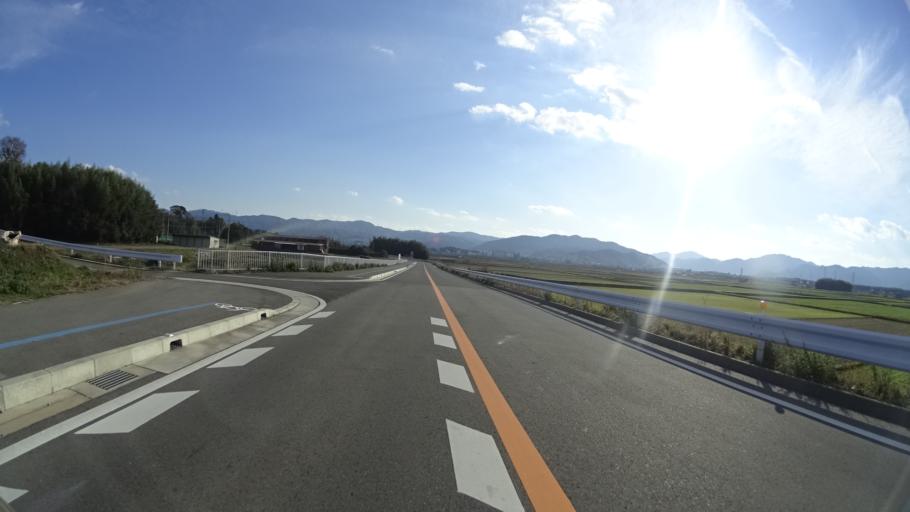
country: JP
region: Kyoto
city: Kameoka
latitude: 35.0353
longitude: 135.5826
